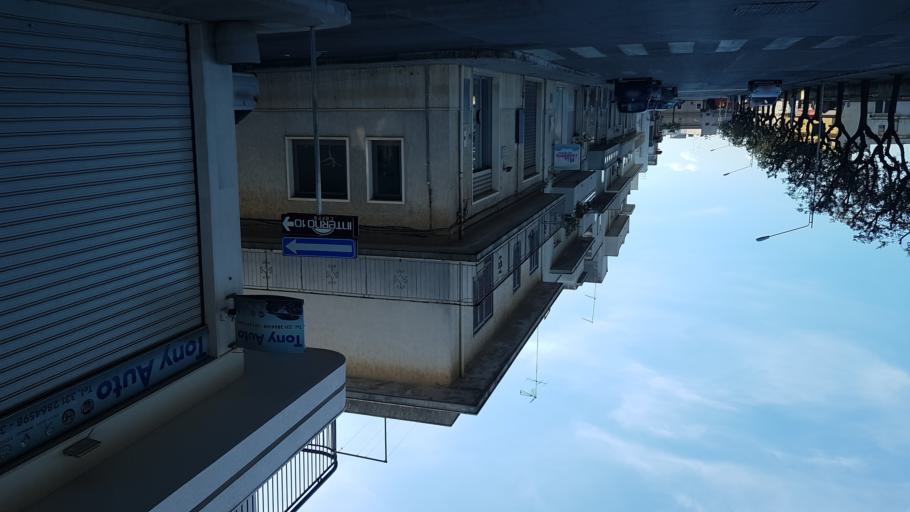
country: IT
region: Apulia
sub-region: Provincia di Brindisi
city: Carovigno
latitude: 40.7057
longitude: 17.6635
